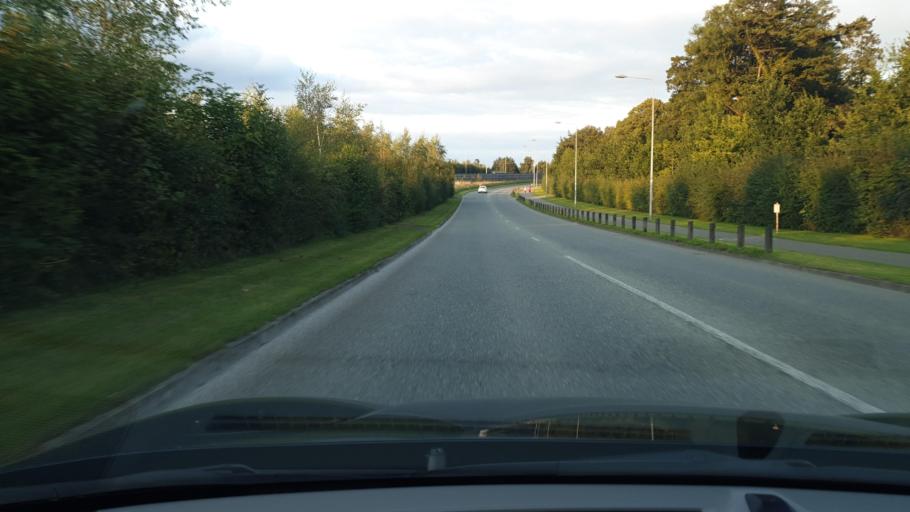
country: IE
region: Leinster
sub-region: Kildare
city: Johnstown
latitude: 53.2413
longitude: -6.6104
